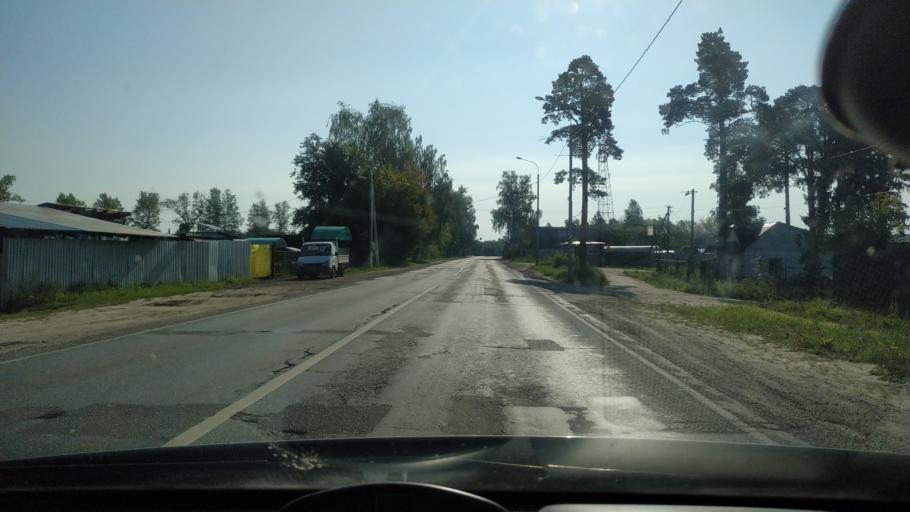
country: RU
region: Moskovskaya
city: Kerva
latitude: 55.5619
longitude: 39.6707
